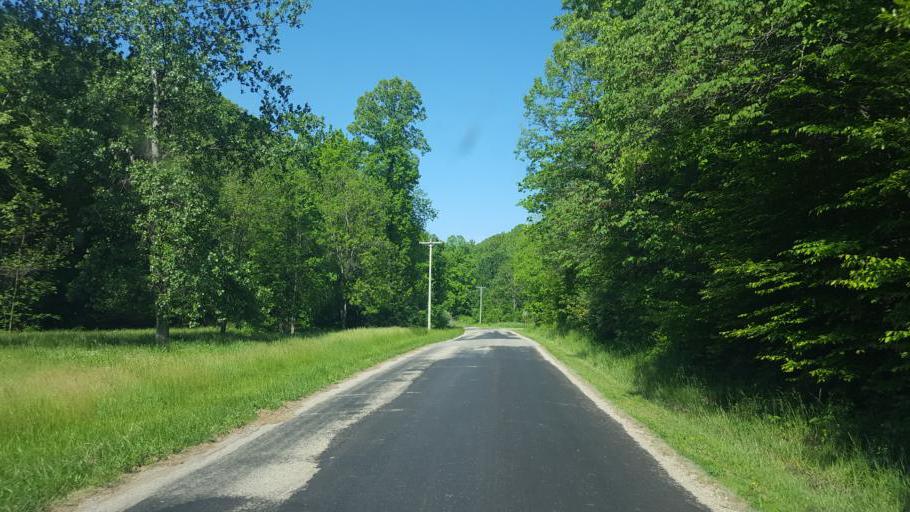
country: US
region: Ohio
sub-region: Jackson County
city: Oak Hill
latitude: 38.9904
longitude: -82.4958
